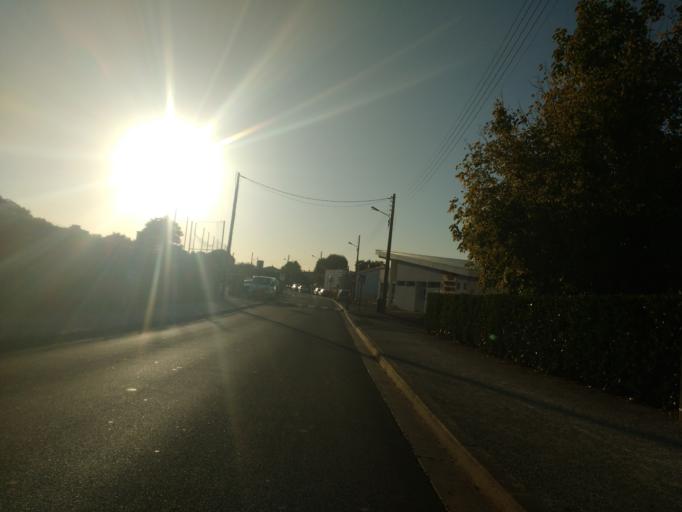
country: FR
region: Aquitaine
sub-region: Departement de la Gironde
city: Pessac
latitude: 44.8134
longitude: -0.6312
